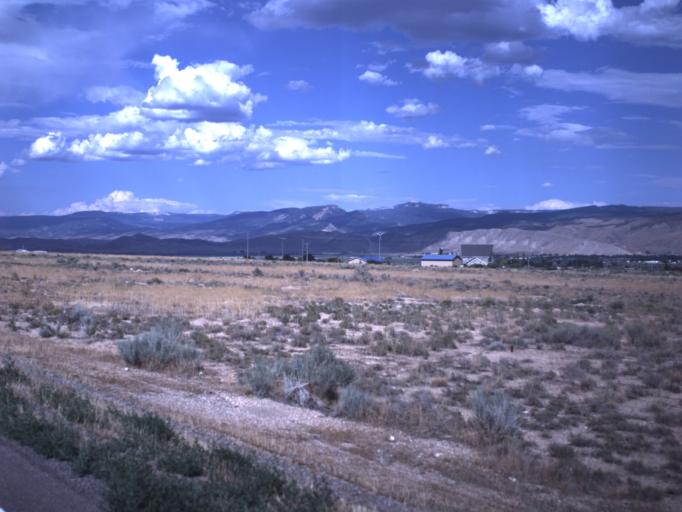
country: US
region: Utah
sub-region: Sevier County
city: Aurora
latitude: 38.9557
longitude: -111.9288
